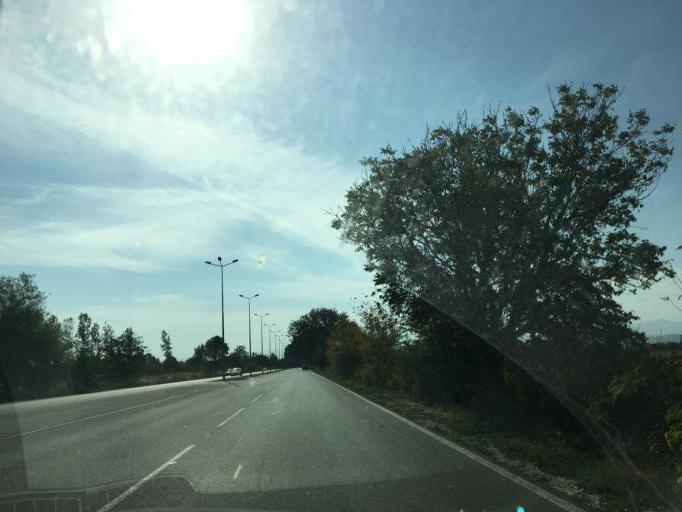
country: BG
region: Pazardzhik
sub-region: Obshtina Pazardzhik
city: Pazardzhik
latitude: 42.2200
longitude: 24.3132
